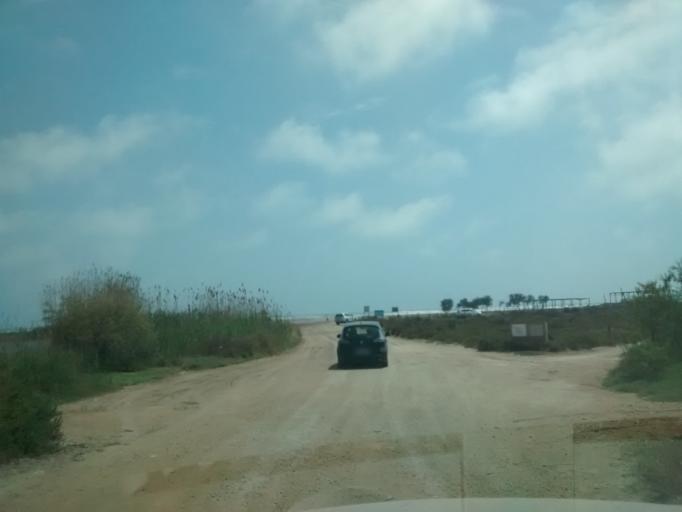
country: ES
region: Catalonia
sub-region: Provincia de Tarragona
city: Deltebre
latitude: 40.6855
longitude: 0.8522
